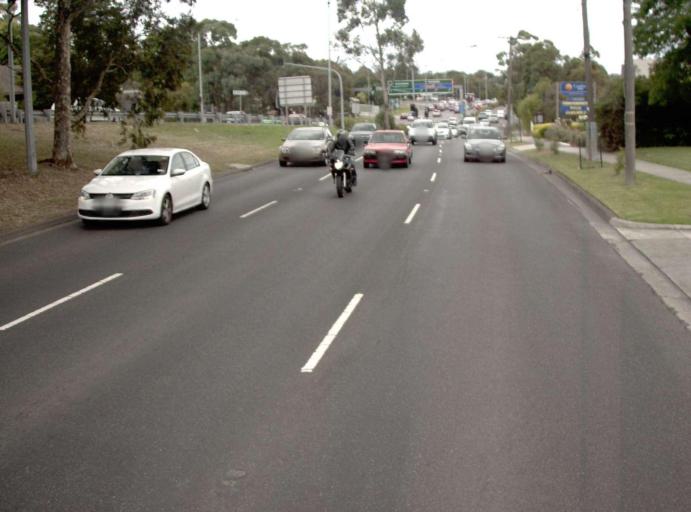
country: AU
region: Victoria
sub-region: Maroondah
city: Ringwood East
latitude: -37.8088
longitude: 145.2399
